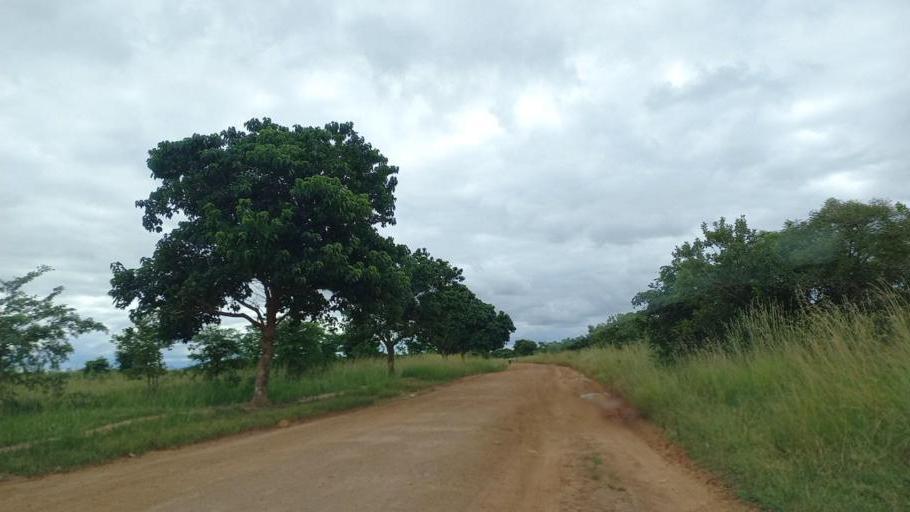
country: ZM
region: Lusaka
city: Chongwe
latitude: -15.4564
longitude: 28.8709
